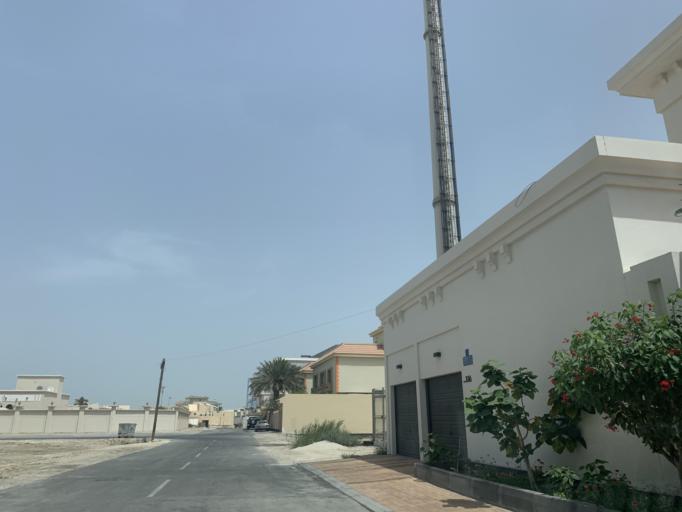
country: BH
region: Northern
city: Madinat `Isa
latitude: 26.1562
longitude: 50.5553
